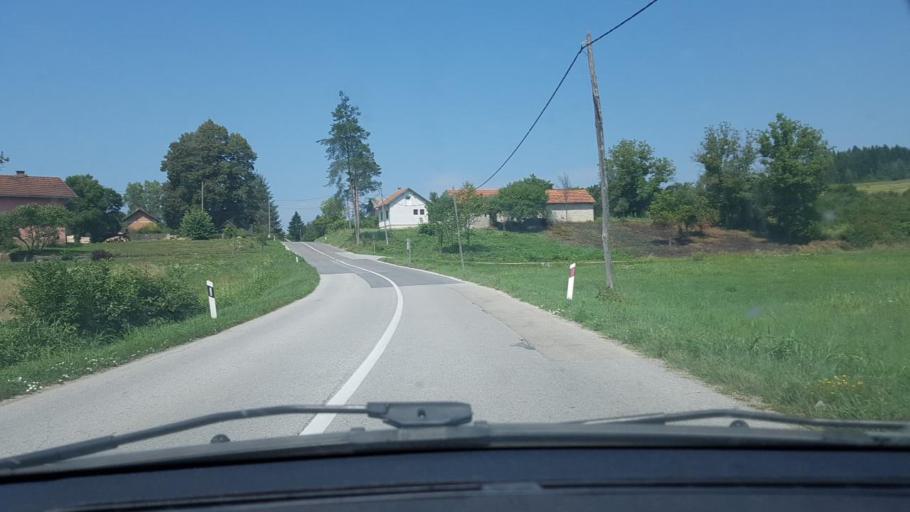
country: BA
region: Federation of Bosnia and Herzegovina
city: Velika Kladusa
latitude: 45.2160
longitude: 15.7572
